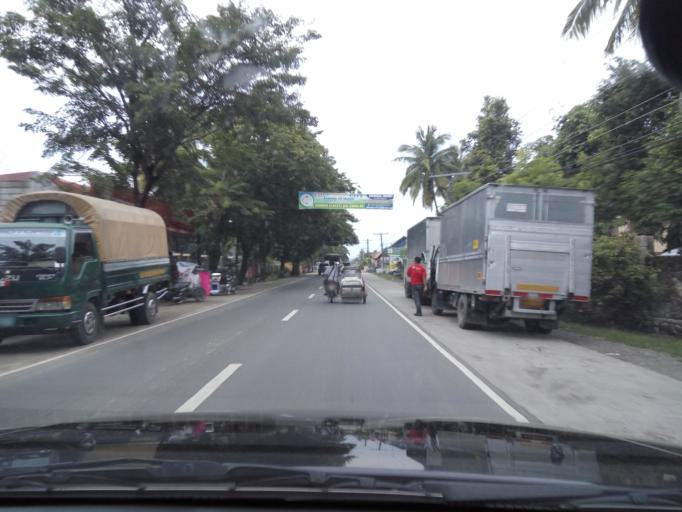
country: PH
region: Central Luzon
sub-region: Province of Nueva Ecija
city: Concepcion
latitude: 15.4488
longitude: 120.8028
